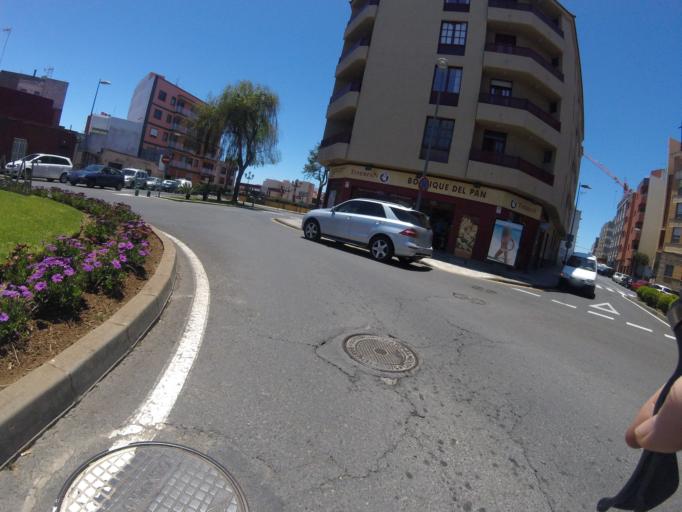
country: ES
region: Canary Islands
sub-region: Provincia de Santa Cruz de Tenerife
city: La Laguna
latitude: 28.4857
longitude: -16.3145
